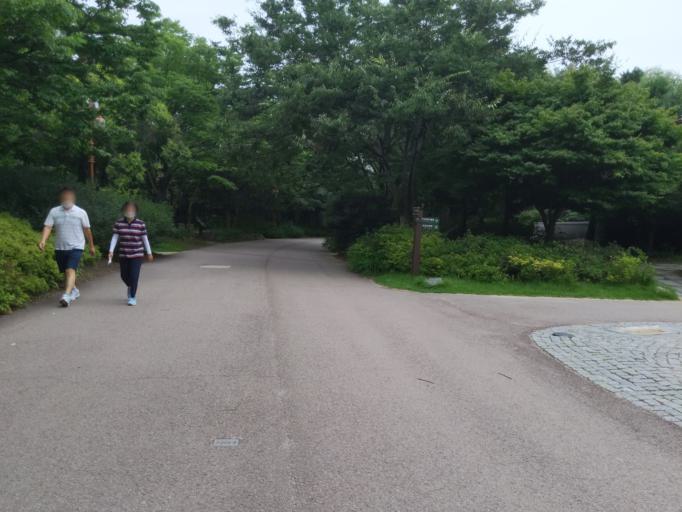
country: KR
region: Daegu
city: Hwawon
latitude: 35.7983
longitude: 128.5247
